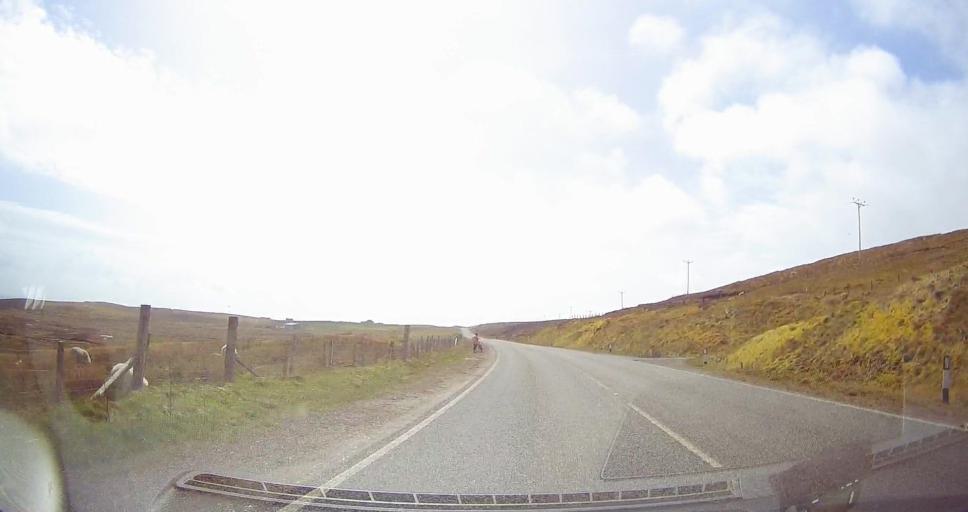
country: GB
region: Scotland
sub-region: Shetland Islands
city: Sandwick
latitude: 60.0853
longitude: -1.2320
